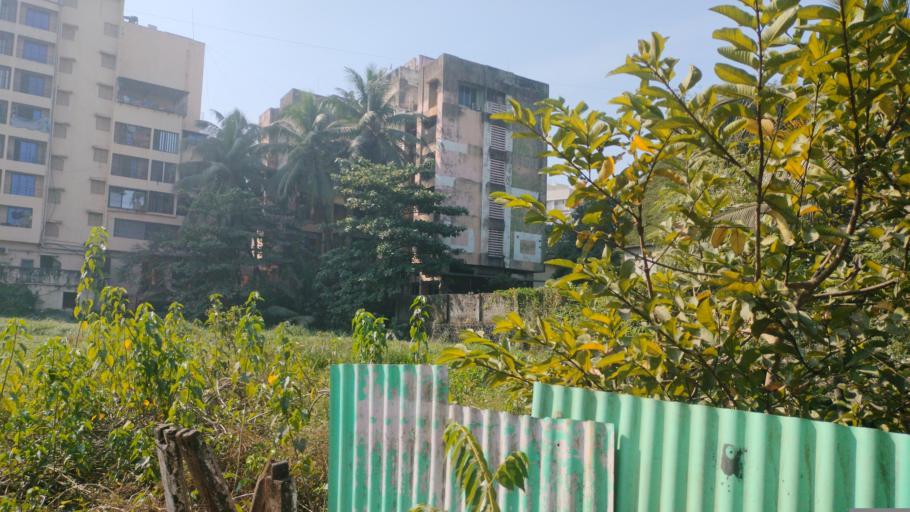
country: IN
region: Maharashtra
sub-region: Thane
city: Thane
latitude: 19.2769
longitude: 72.9607
